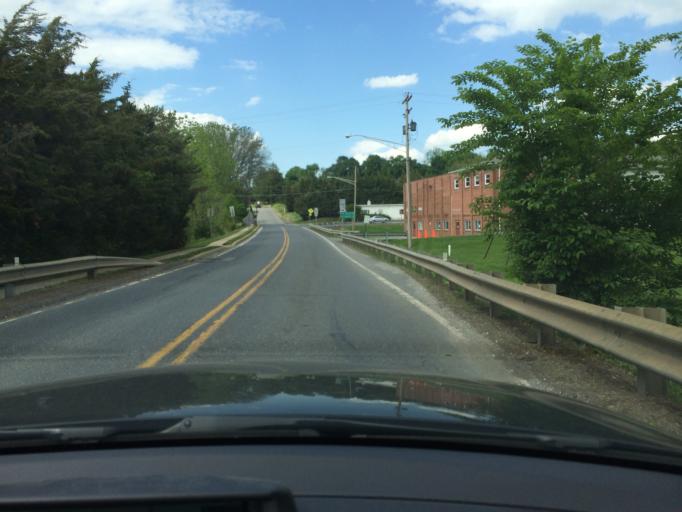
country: US
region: Maryland
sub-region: Carroll County
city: New Windsor
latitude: 39.5726
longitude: -77.1762
